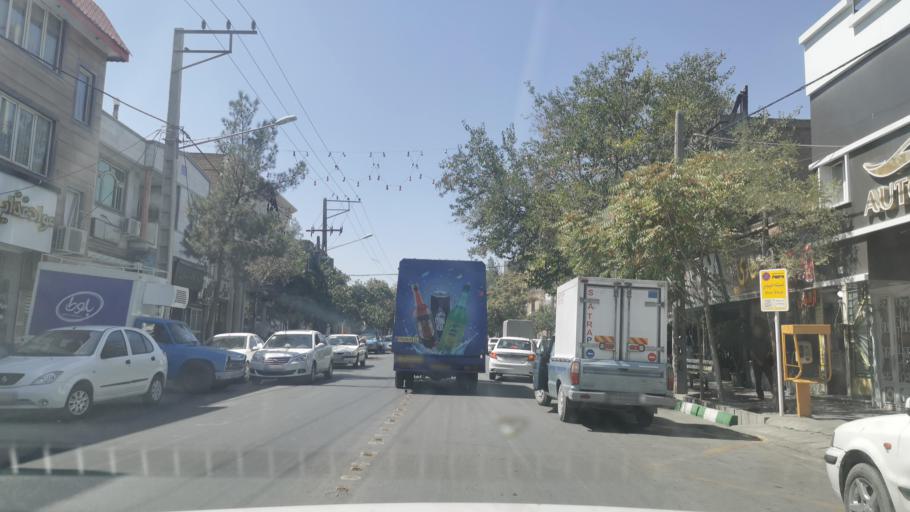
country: IR
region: Razavi Khorasan
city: Mashhad
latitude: 36.3583
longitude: 59.5454
